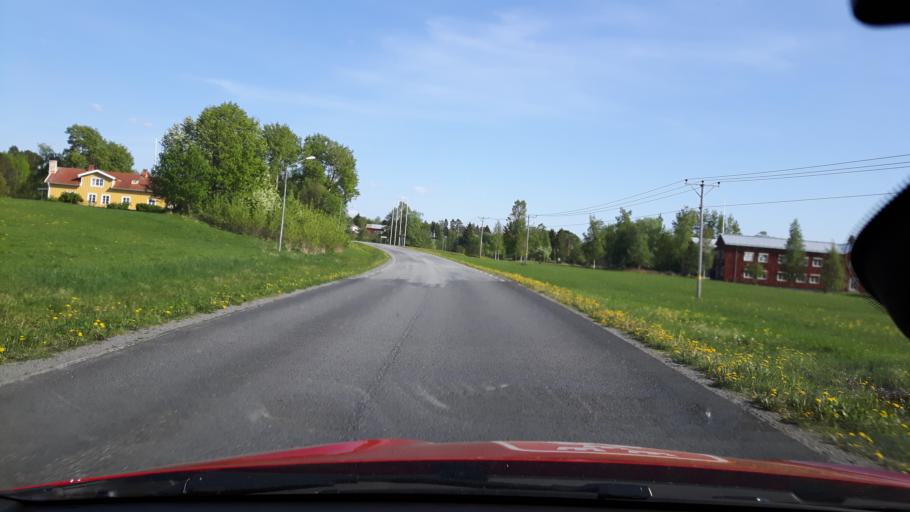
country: SE
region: Jaemtland
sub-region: Bergs Kommun
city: Hoverberg
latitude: 62.9416
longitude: 14.4986
